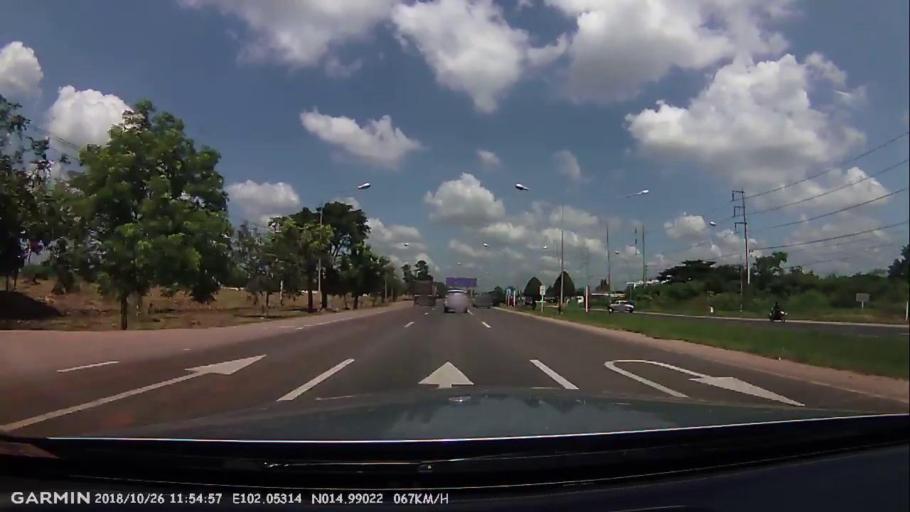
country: TH
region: Nakhon Ratchasima
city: Nakhon Ratchasima
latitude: 14.9904
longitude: 102.0532
